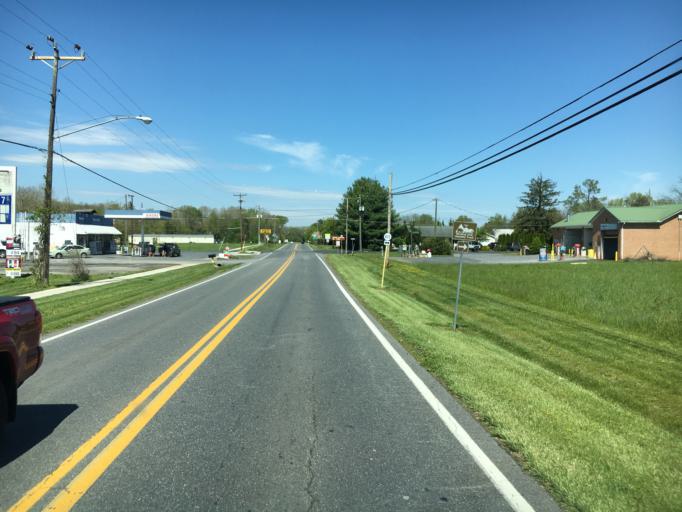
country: US
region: Virginia
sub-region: Rockingham County
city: Grottoes
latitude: 38.2630
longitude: -78.8274
